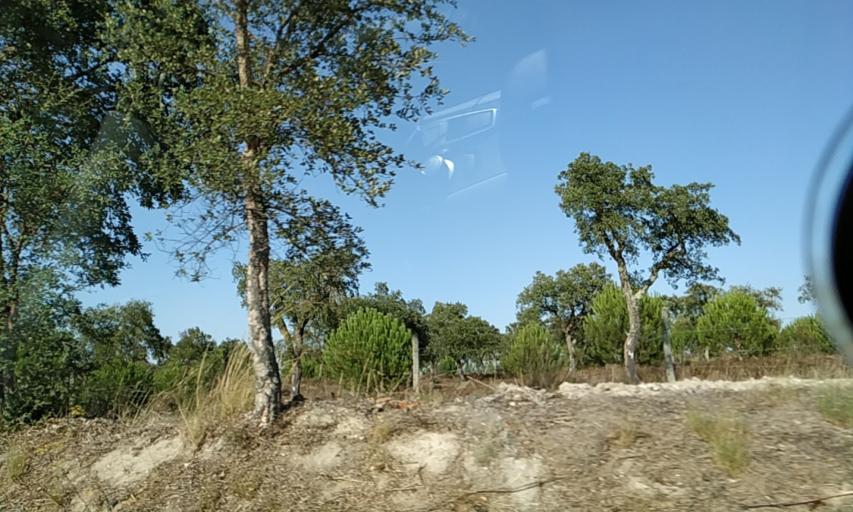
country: PT
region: Santarem
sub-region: Coruche
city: Coruche
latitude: 39.0375
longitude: -8.5609
